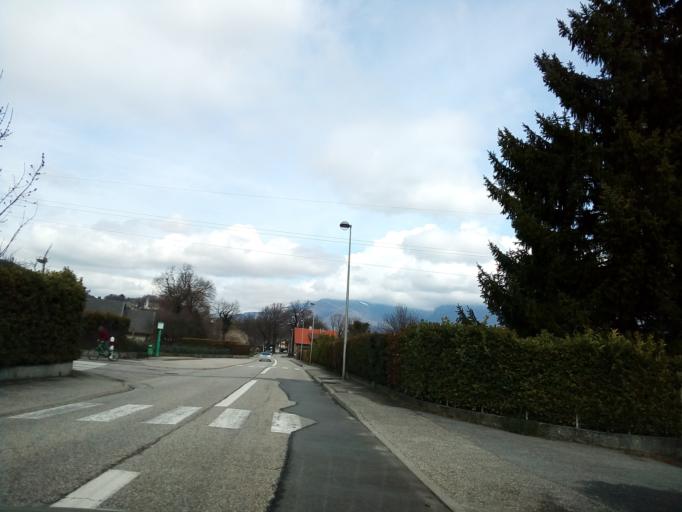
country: FR
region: Rhone-Alpes
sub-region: Departement de la Savoie
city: Saint-Baldoph
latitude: 45.5263
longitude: 5.9553
